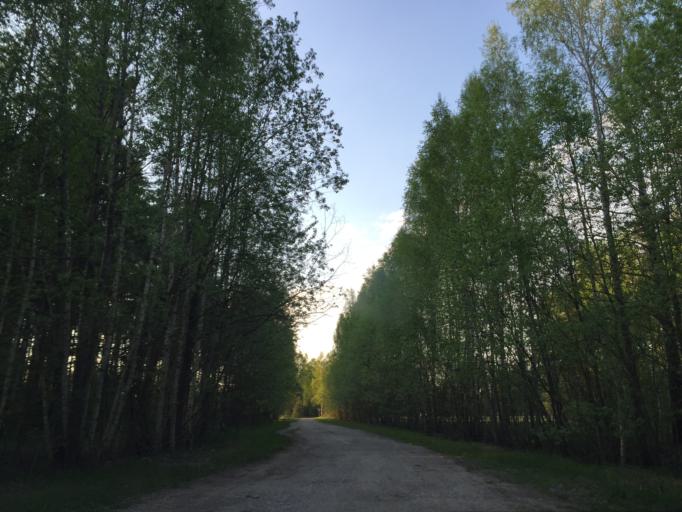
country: LV
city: Tireli
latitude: 56.8899
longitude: 23.6896
